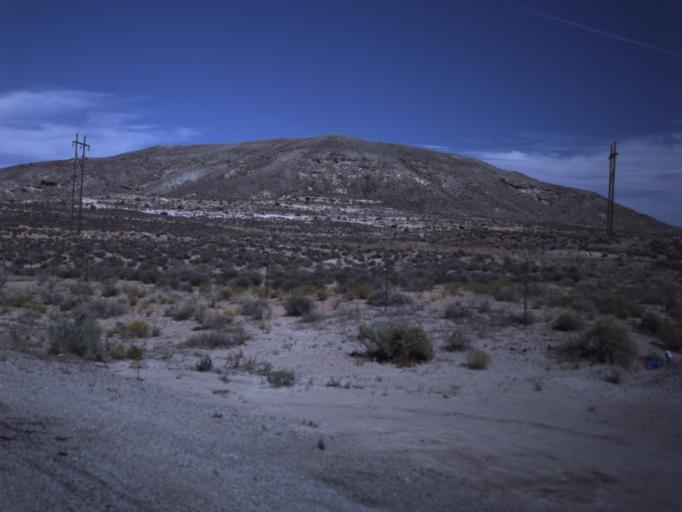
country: US
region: Utah
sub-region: San Juan County
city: Blanding
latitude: 37.2774
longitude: -109.3612
